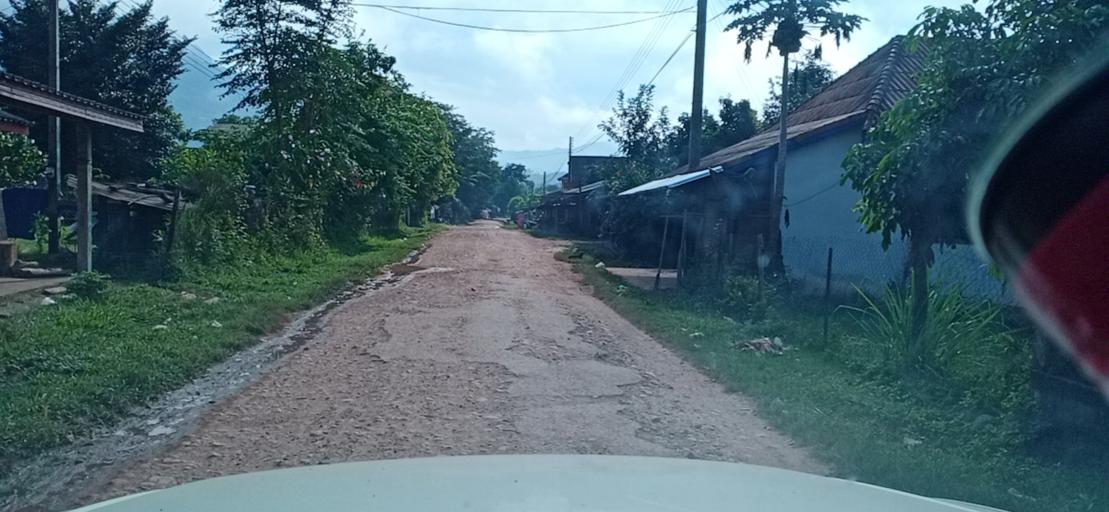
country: TH
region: Changwat Bueng Kan
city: Pak Khat
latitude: 18.6779
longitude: 103.1901
